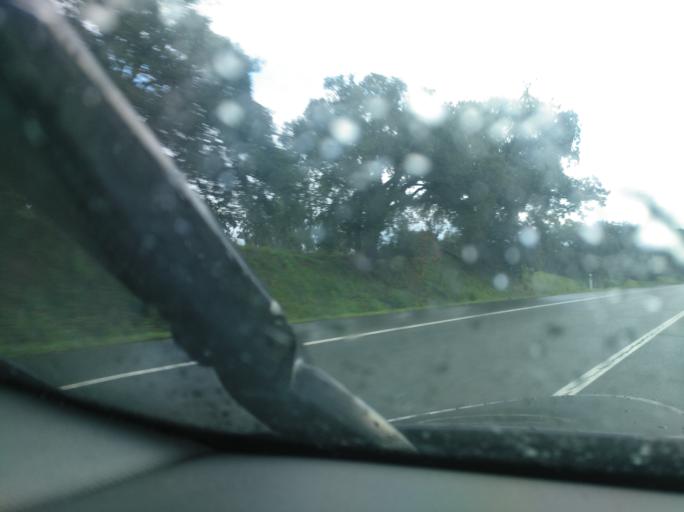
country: PT
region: Setubal
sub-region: Grandola
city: Grandola
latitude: 38.0786
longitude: -8.4169
